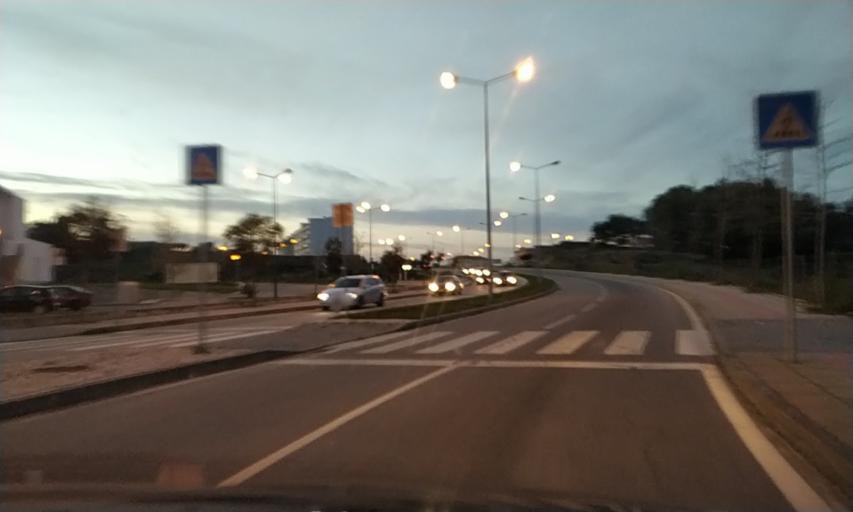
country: PT
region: Castelo Branco
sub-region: Castelo Branco
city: Castelo Branco
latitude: 39.8314
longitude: -7.4868
